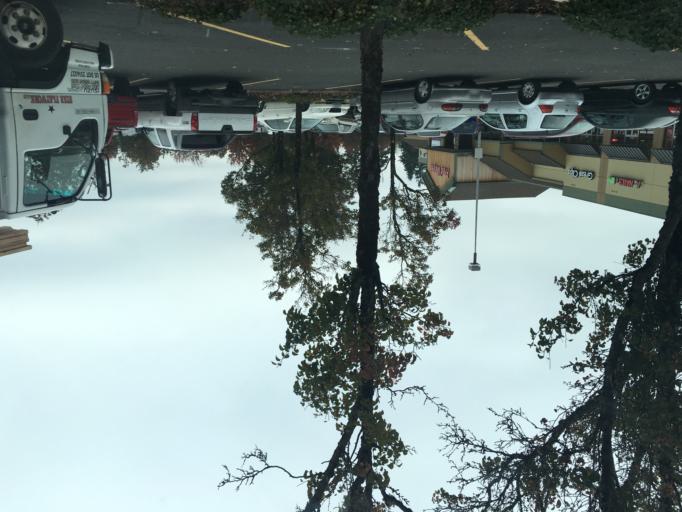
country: US
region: Oregon
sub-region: Multnomah County
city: Lents
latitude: 45.4578
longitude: -122.5799
